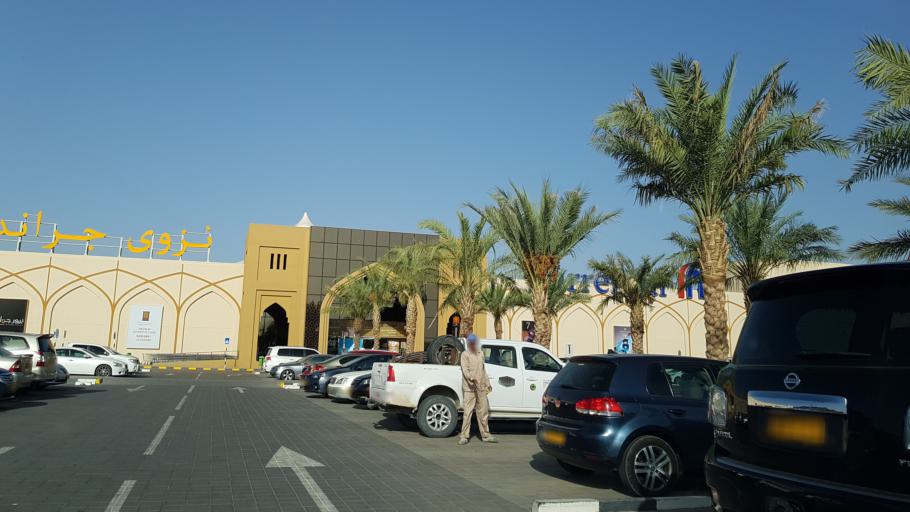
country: OM
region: Muhafazat ad Dakhiliyah
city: Nizwa
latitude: 22.8714
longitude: 57.5363
